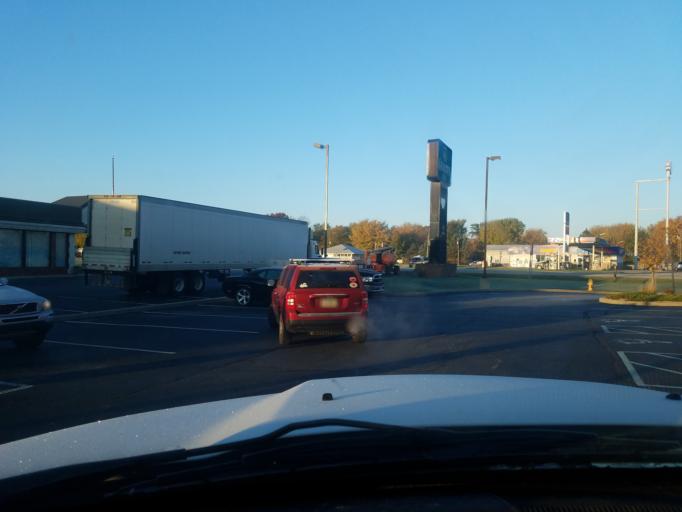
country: US
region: Indiana
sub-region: Montgomery County
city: Crawfordsville
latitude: 40.0741
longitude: -86.9050
